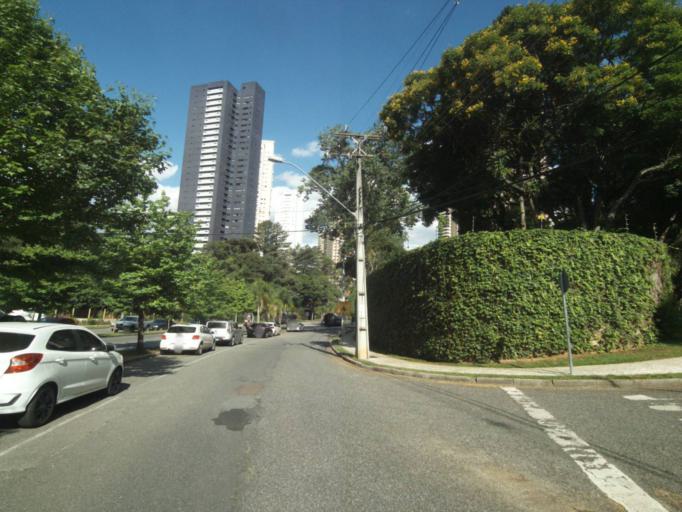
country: BR
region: Parana
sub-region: Curitiba
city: Curitiba
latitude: -25.4365
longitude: -49.3294
